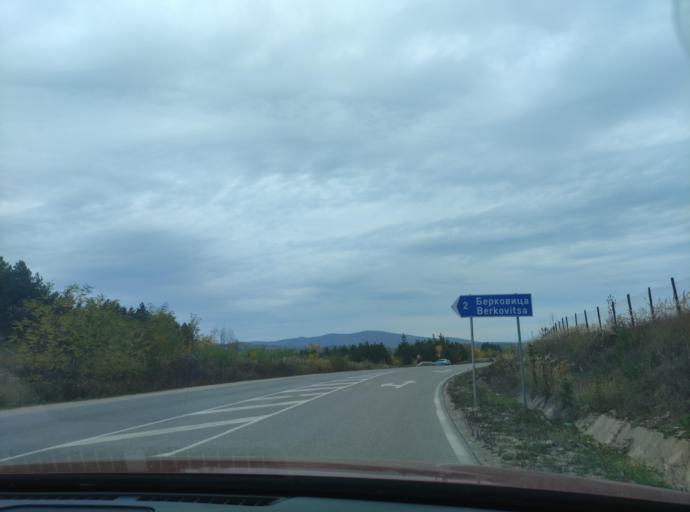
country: BG
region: Montana
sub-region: Obshtina Berkovitsa
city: Berkovitsa
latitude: 43.2245
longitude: 23.1567
